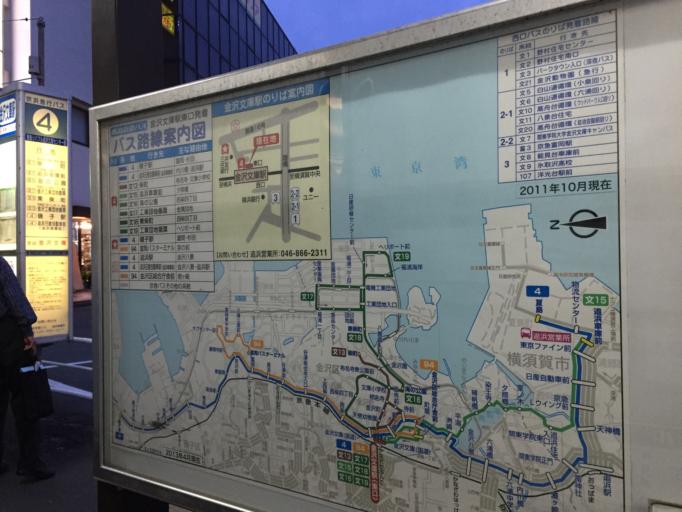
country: JP
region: Kanagawa
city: Zushi
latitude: 35.3434
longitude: 139.6219
